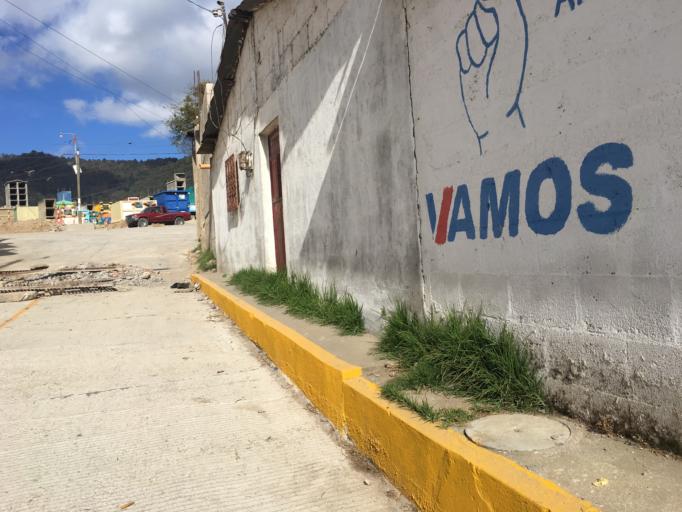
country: GT
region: Quetzaltenango
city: Ostuncalco
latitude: 14.8671
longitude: -91.6253
